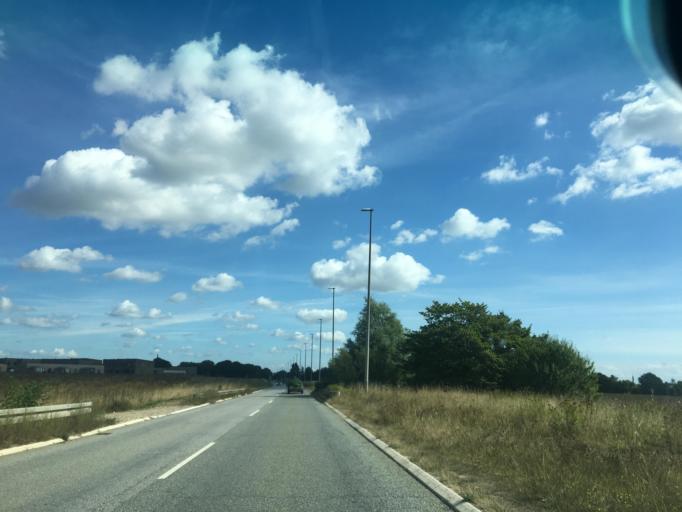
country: DK
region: Zealand
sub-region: Greve Kommune
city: Greve
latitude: 55.5754
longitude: 12.2563
